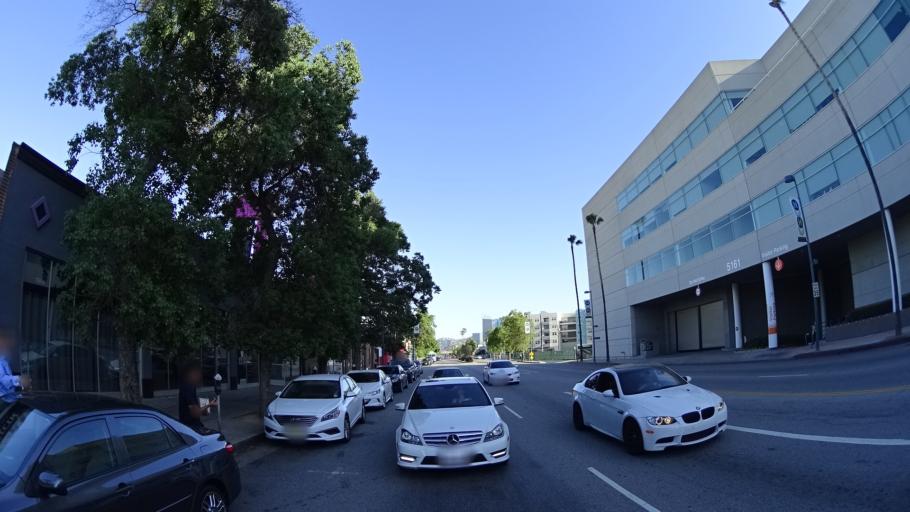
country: US
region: California
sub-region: Los Angeles County
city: North Hollywood
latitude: 34.1644
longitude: -118.3743
